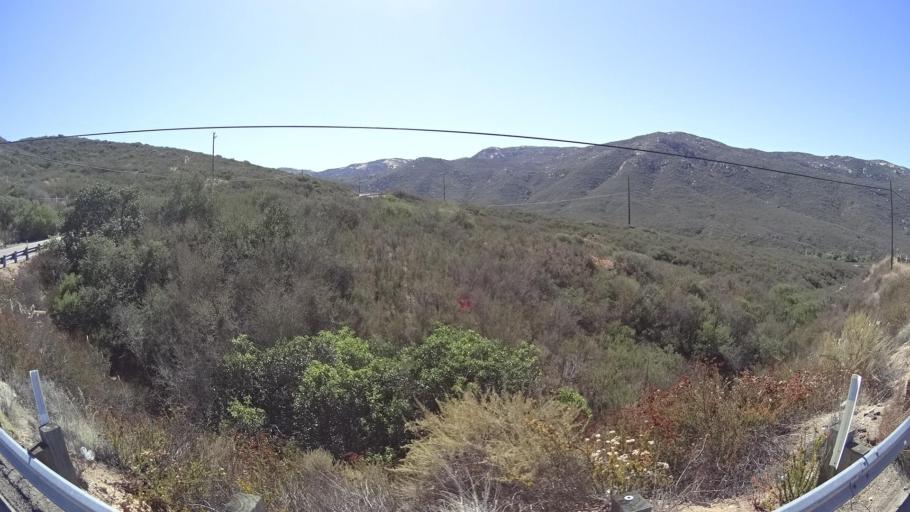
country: US
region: California
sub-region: San Diego County
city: Alpine
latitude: 32.7916
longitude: -116.7332
